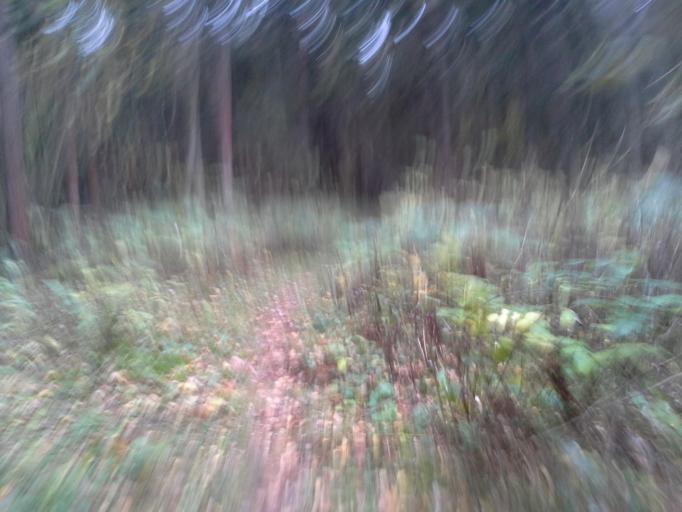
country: RU
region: Moskovskaya
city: Gorki Vtoryye
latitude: 55.6896
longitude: 37.1614
